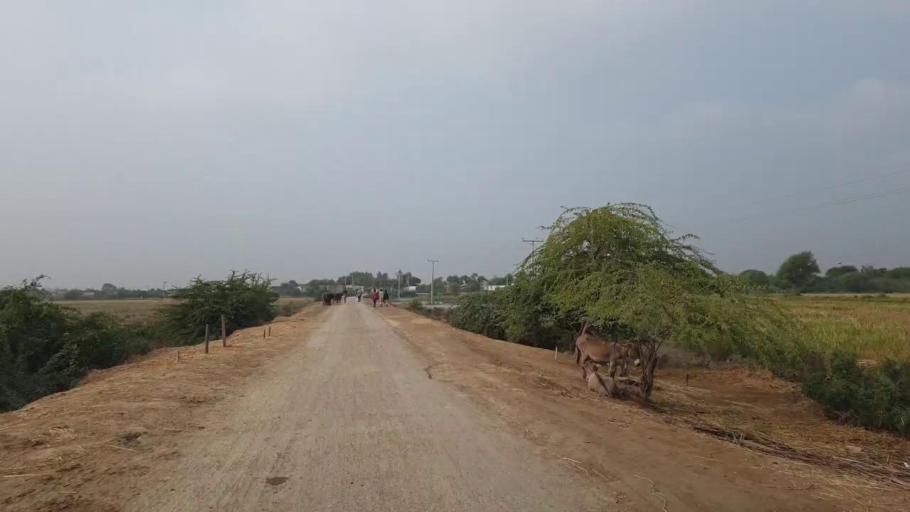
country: PK
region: Sindh
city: Matli
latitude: 24.9627
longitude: 68.5874
